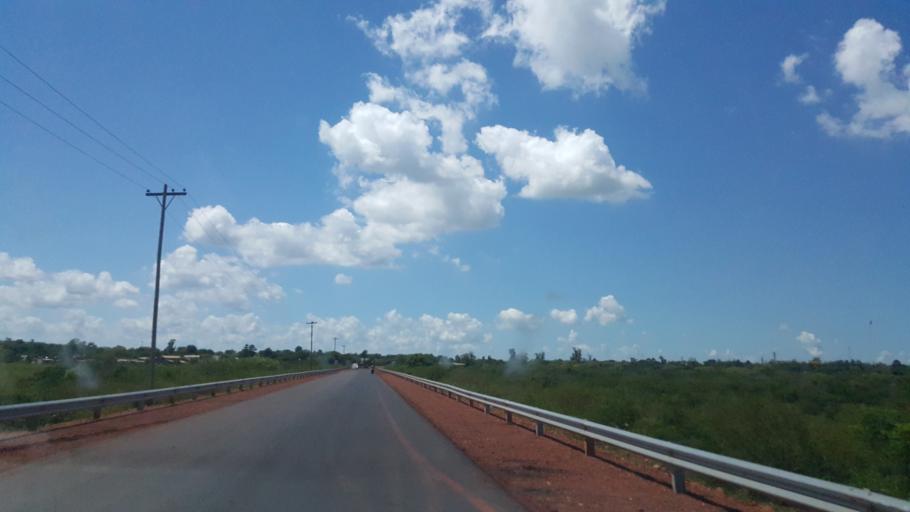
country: AR
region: Corrientes
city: Santo Tome
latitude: -28.5375
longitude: -56.0511
